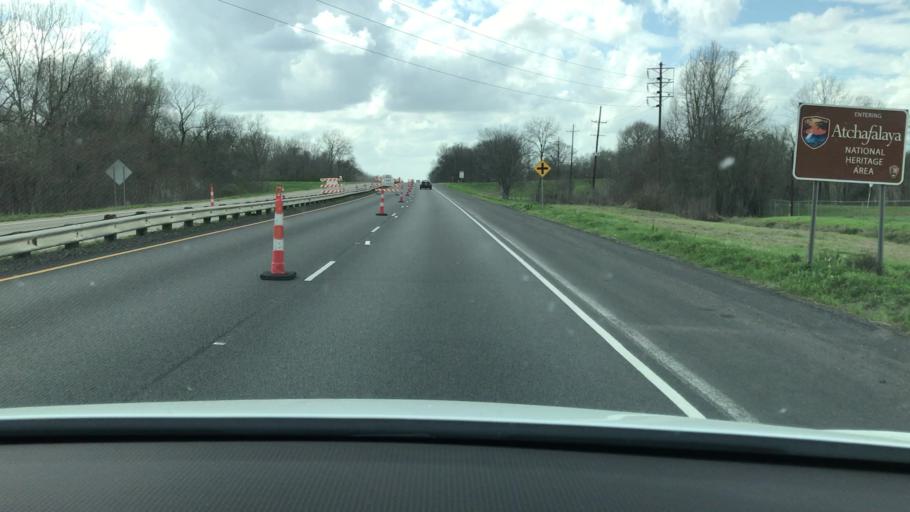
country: US
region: Louisiana
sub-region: Pointe Coupee Parish
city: Livonia
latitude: 30.5571
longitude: -91.6551
